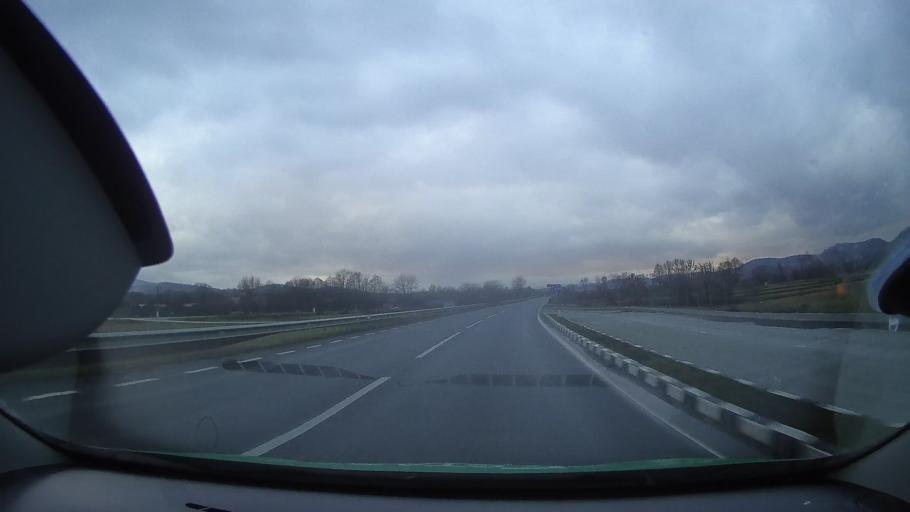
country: RO
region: Hunedoara
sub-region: Comuna Baia de Cris
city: Baia de Cris
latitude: 46.1696
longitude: 22.7292
